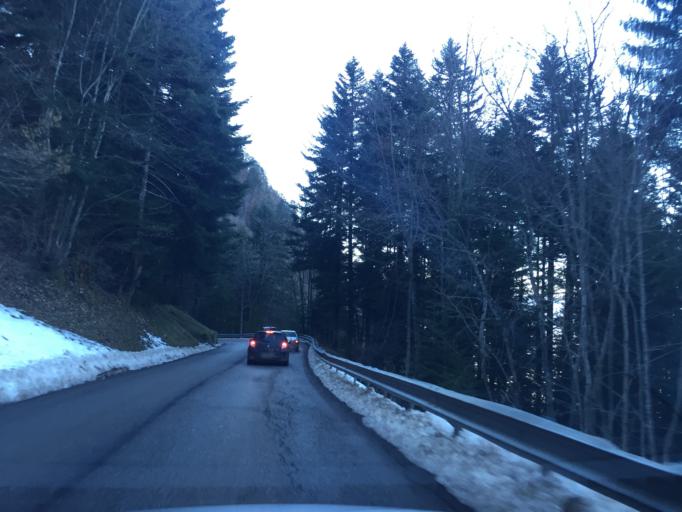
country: FR
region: Rhone-Alpes
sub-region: Departement de la Haute-Savoie
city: Cusy
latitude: 45.7014
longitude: 6.0046
